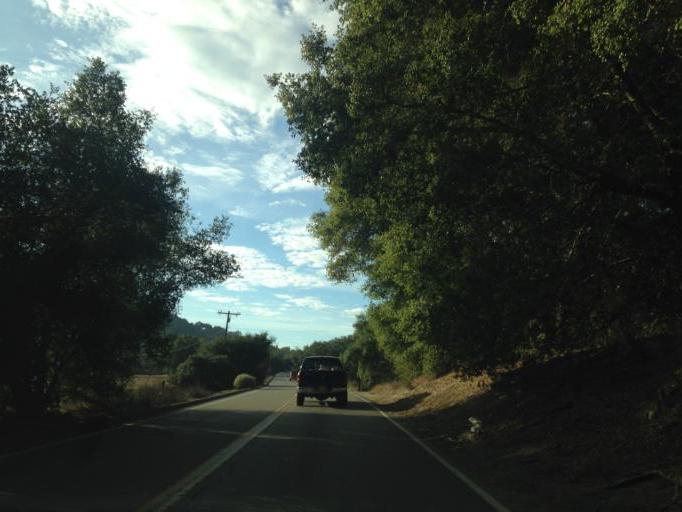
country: US
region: California
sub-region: San Diego County
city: Rainbow
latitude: 33.4355
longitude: -117.0895
